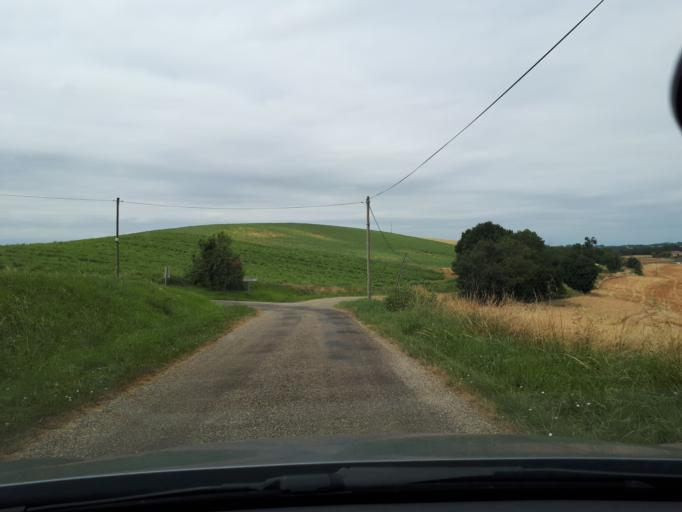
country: FR
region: Midi-Pyrenees
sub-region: Departement du Gers
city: Valence-sur-Baise
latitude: 43.9144
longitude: 0.4918
